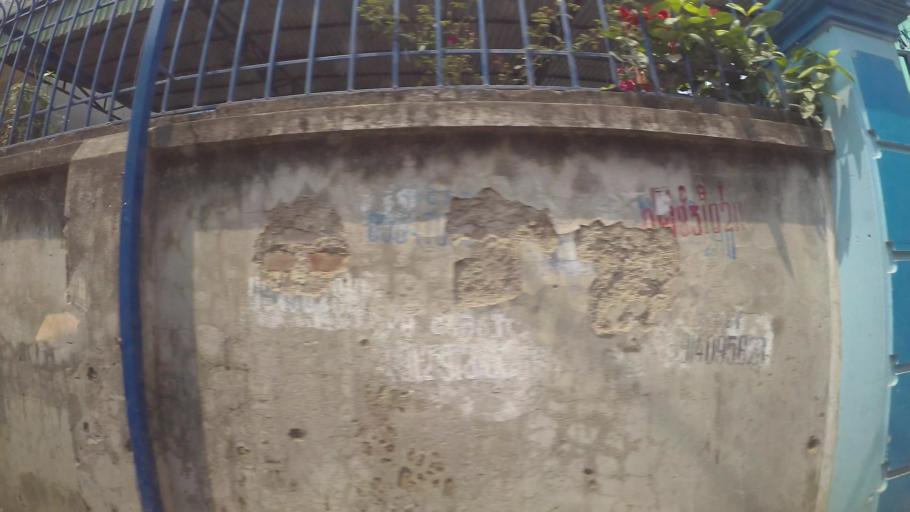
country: VN
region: Ha Noi
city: Van Dien
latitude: 20.9535
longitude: 105.8249
